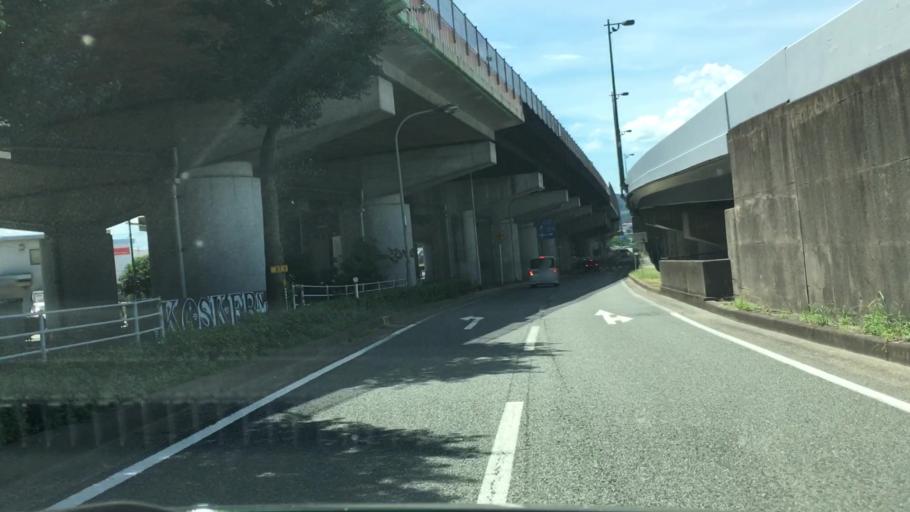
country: JP
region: Fukuoka
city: Onojo
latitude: 33.5258
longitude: 130.4956
